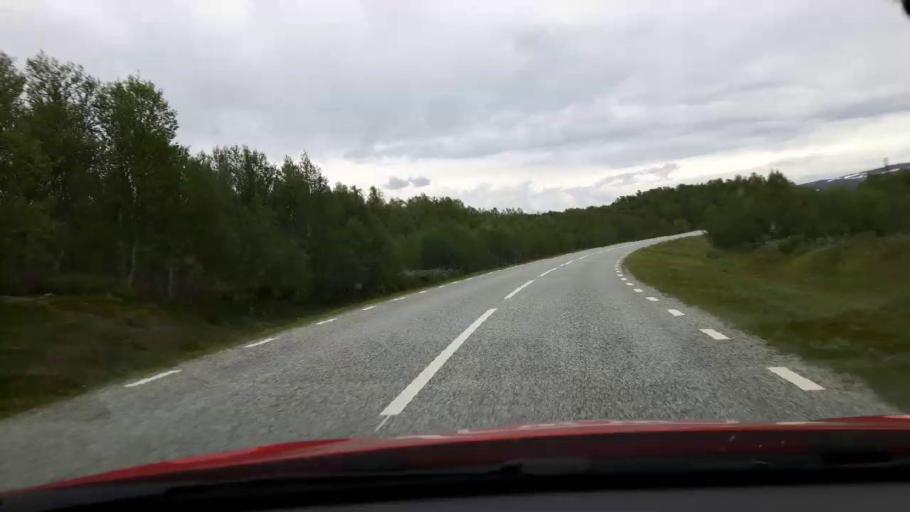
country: NO
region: Sor-Trondelag
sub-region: Tydal
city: Aas
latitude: 62.6265
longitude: 12.1288
